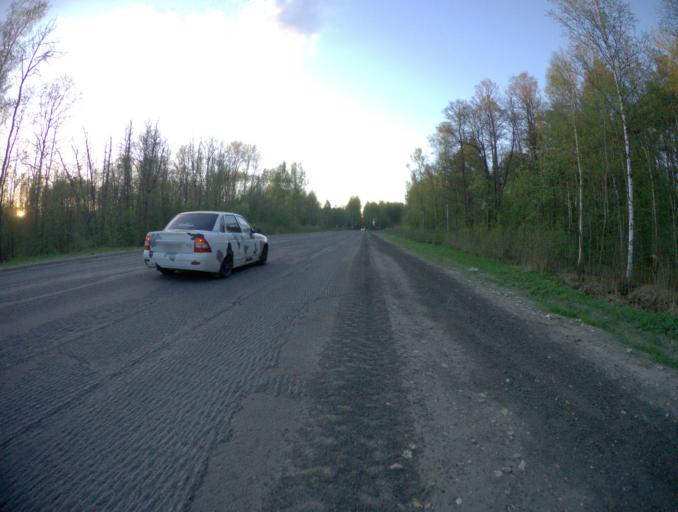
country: RU
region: Vladimir
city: Kommunar
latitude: 56.0913
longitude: 40.4374
